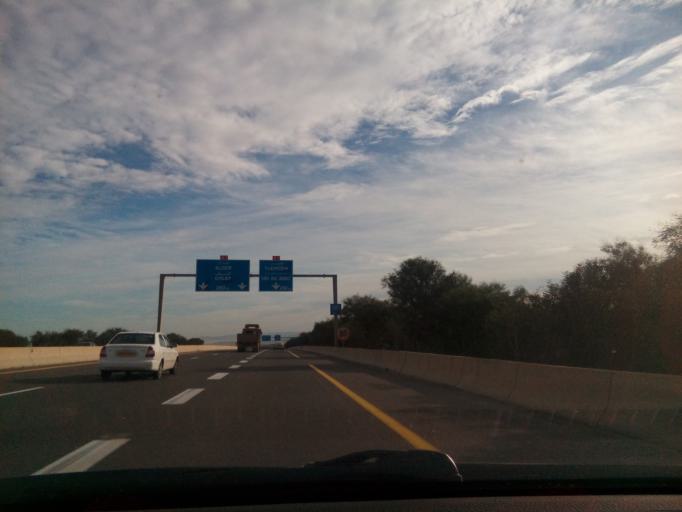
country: DZ
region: Mascara
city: Sig
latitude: 35.5419
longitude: -0.3496
